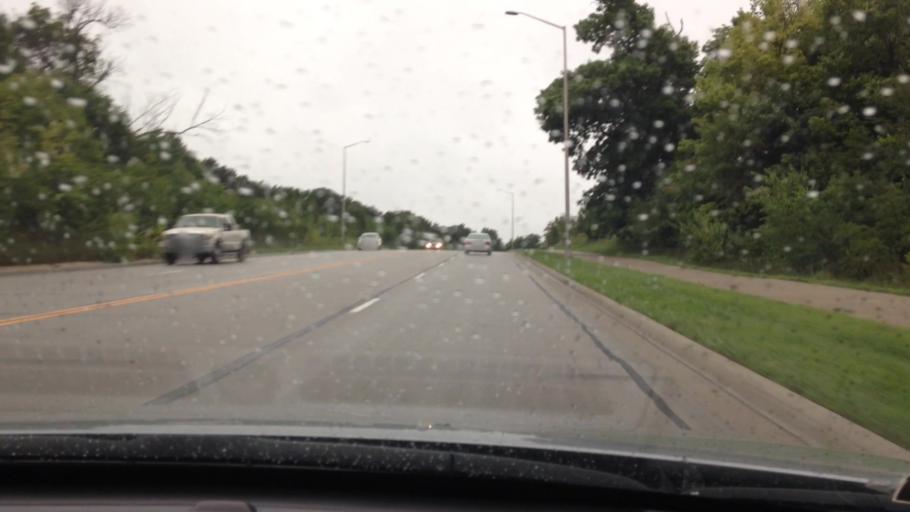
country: US
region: Kansas
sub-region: Leavenworth County
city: Leavenworth
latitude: 39.2975
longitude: -94.9518
